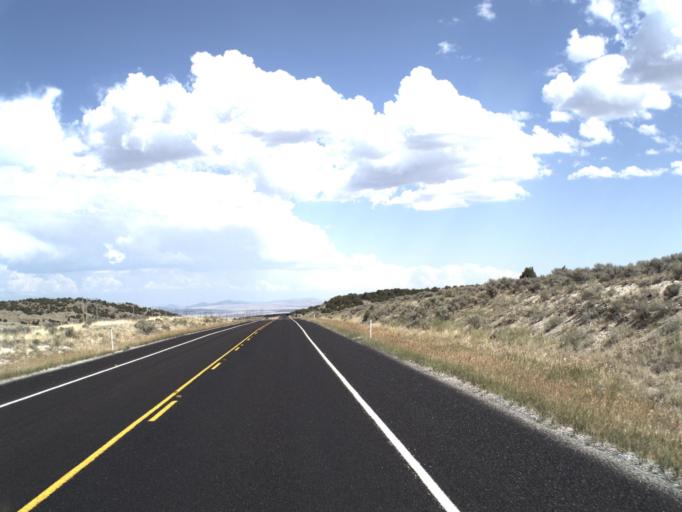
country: US
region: Idaho
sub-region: Minidoka County
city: Rupert
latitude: 41.9867
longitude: -113.1777
